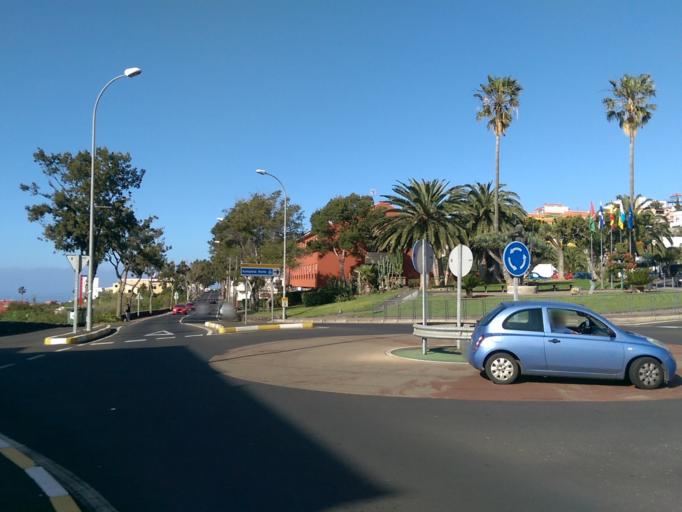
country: ES
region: Canary Islands
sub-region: Provincia de Santa Cruz de Tenerife
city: La Matanza de Acentejo
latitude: 28.4482
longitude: -16.4580
